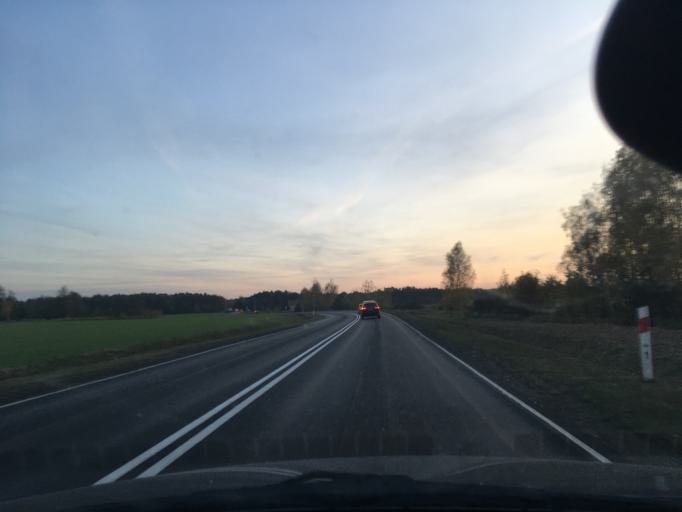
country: PL
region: Masovian Voivodeship
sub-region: Powiat plocki
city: Wyszogrod
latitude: 52.3534
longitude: 20.2090
